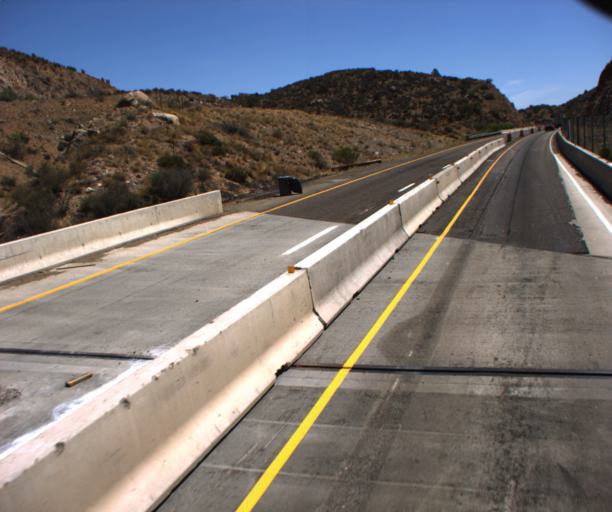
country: US
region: Arizona
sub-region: Mohave County
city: Peach Springs
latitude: 35.1720
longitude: -113.5073
